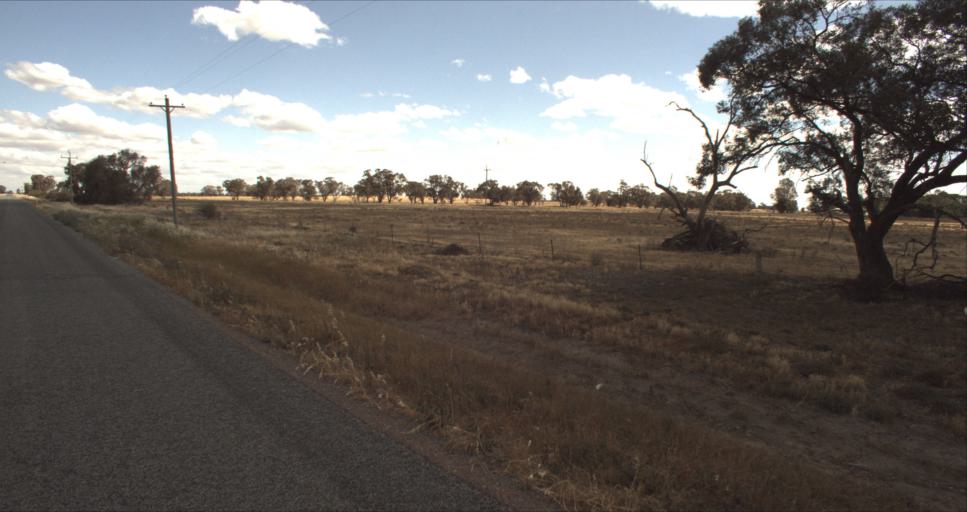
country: AU
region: New South Wales
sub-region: Leeton
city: Leeton
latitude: -34.4862
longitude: 146.2481
